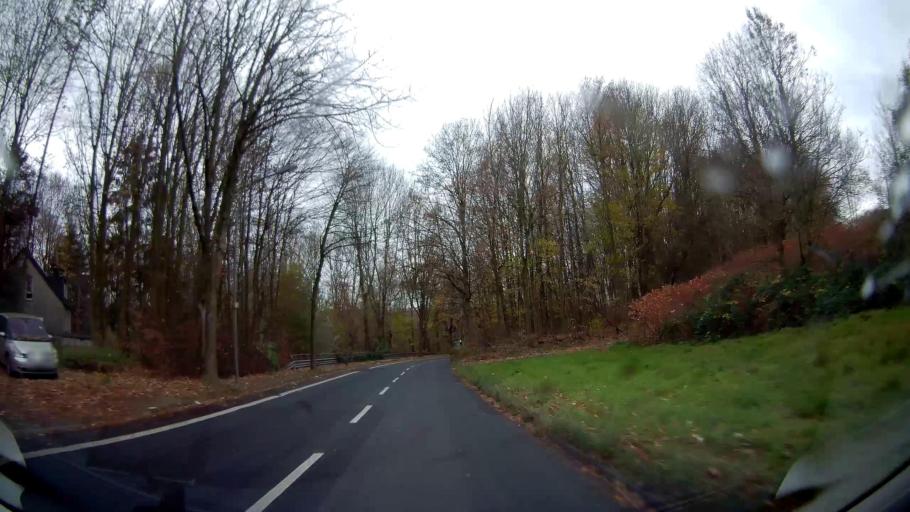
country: DE
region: North Rhine-Westphalia
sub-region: Regierungsbezirk Arnsberg
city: Bochum
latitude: 51.5024
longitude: 7.2306
